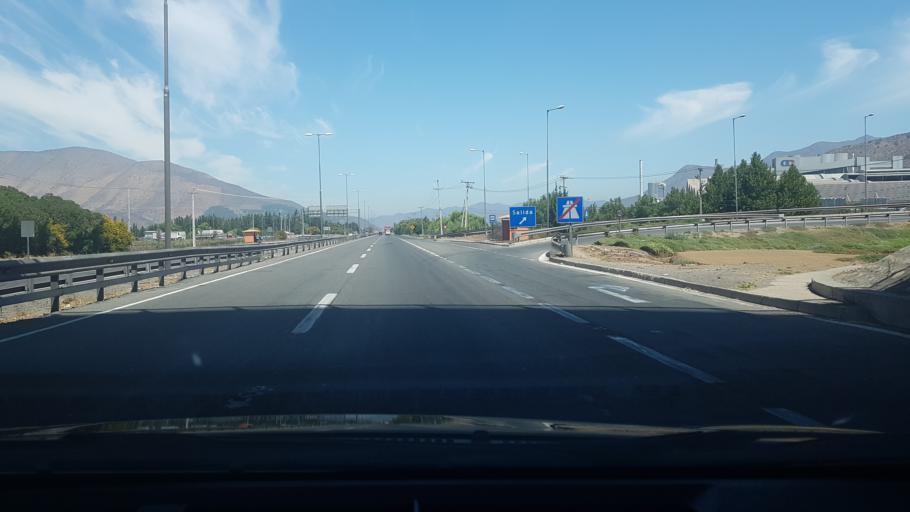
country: CL
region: Valparaiso
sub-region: Provincia de San Felipe
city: Llaillay
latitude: -32.8510
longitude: -70.9428
